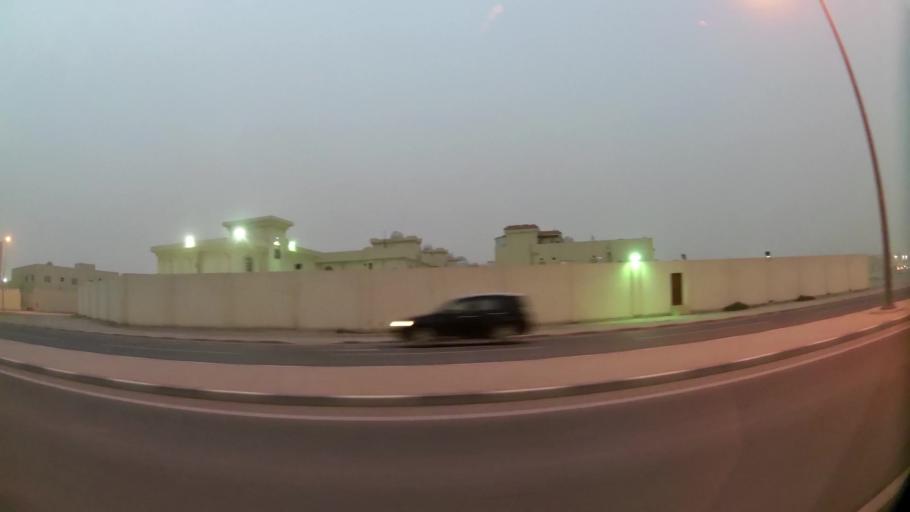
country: QA
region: Baladiyat ad Dawhah
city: Doha
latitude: 25.2331
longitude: 51.4923
